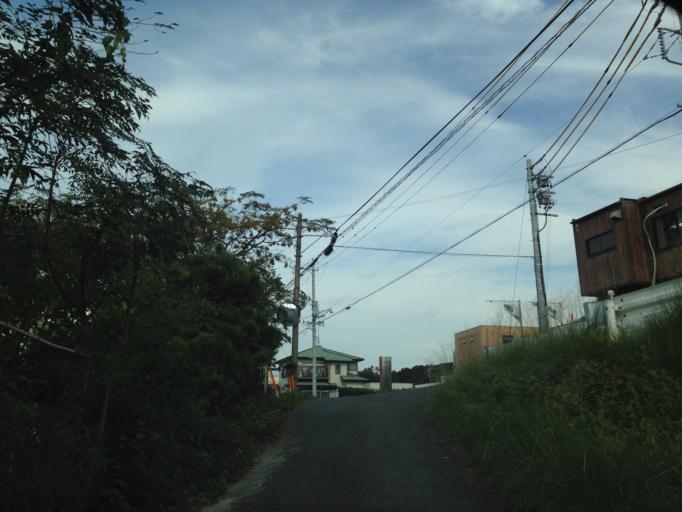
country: JP
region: Shizuoka
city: Iwata
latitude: 34.7237
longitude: 137.8630
